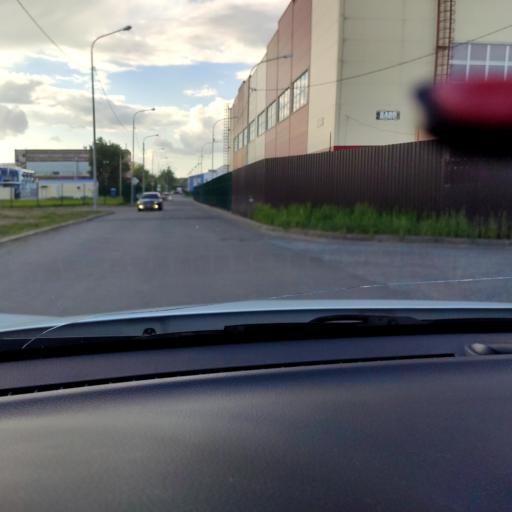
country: RU
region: Tatarstan
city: Staroye Arakchino
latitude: 55.8304
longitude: 49.0370
